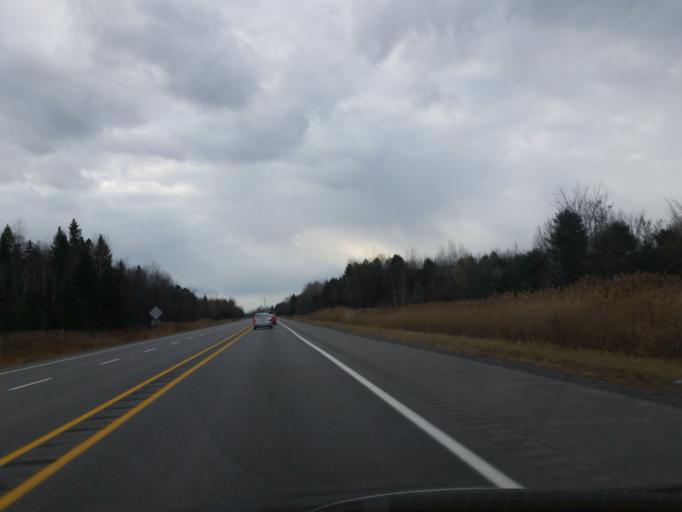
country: CA
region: Quebec
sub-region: Laurentides
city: Saint-Colomban
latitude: 45.6804
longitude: -74.1572
